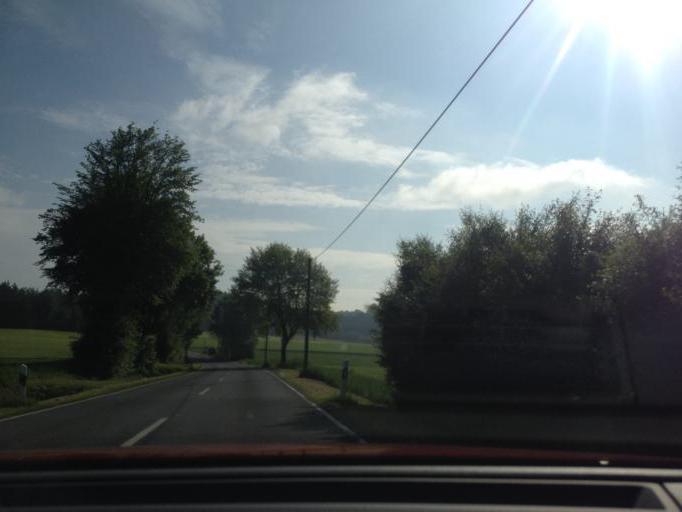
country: DE
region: Bavaria
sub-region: Upper Palatinate
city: Speinshart
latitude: 49.7891
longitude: 11.8286
